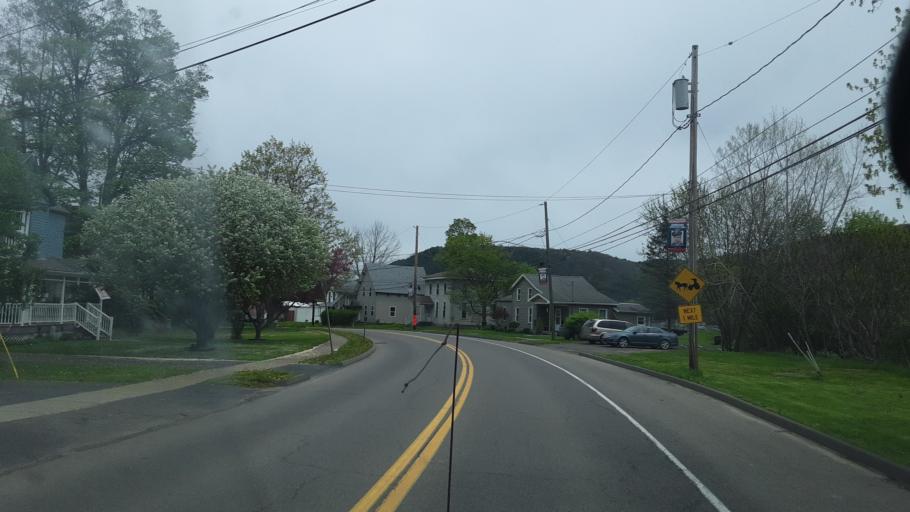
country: US
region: New York
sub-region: Steuben County
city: Addison
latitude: 42.1031
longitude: -77.2374
